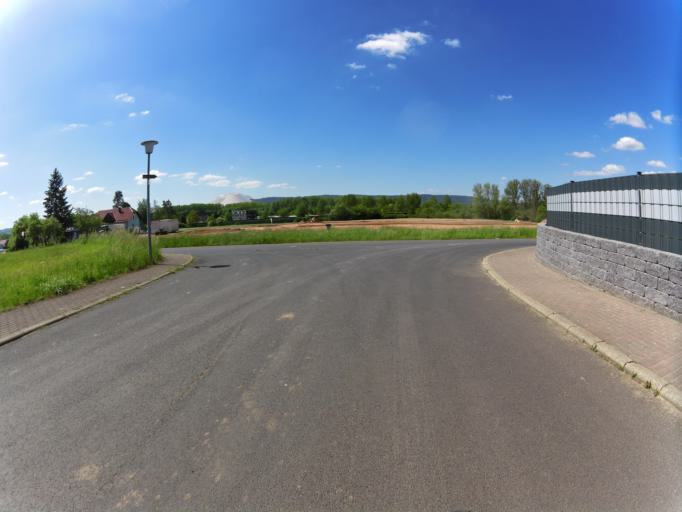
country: DE
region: Thuringia
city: Dankmarshausen
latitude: 50.9527
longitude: 10.0212
